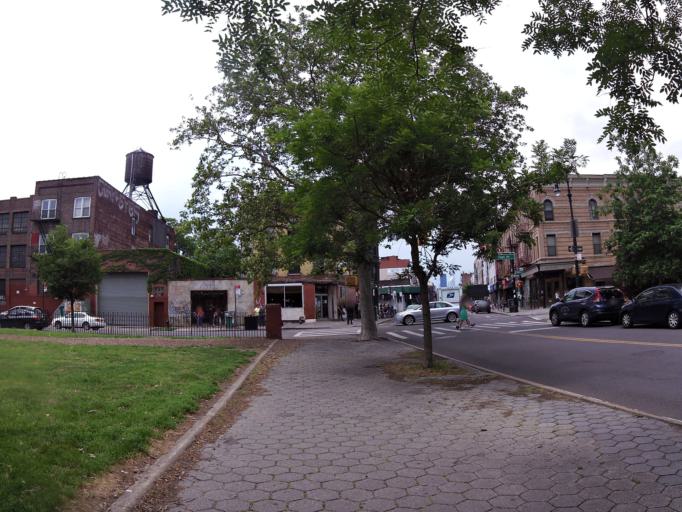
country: US
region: New York
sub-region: Queens County
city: Long Island City
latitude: 40.7219
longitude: -73.9497
